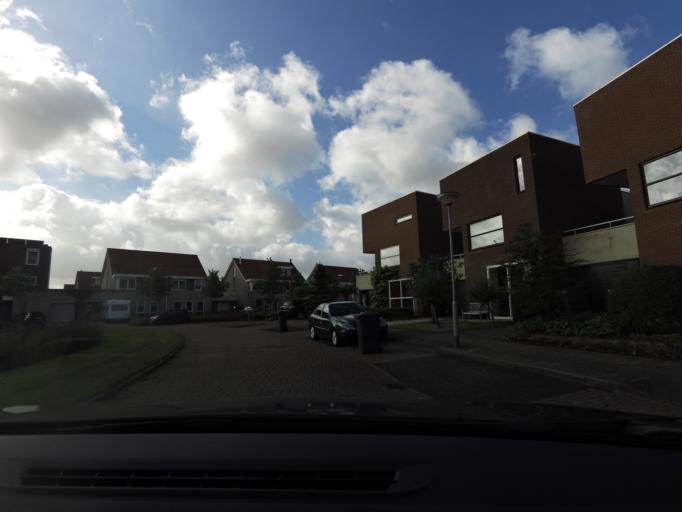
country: NL
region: Zeeland
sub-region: Schouwen-Duiveland
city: Scharendijke
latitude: 51.6455
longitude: 3.8990
